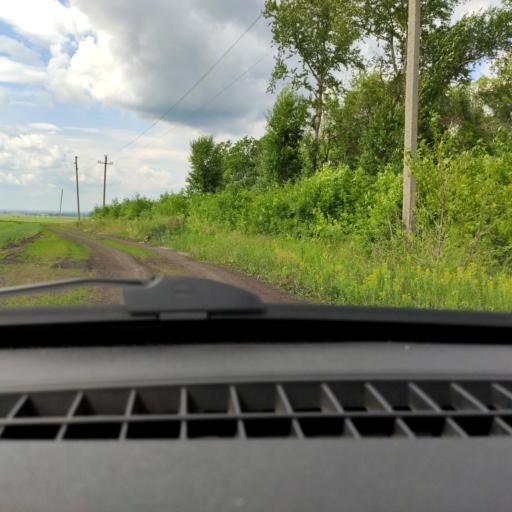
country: RU
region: Bashkortostan
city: Kabakovo
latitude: 54.5252
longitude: 56.0626
